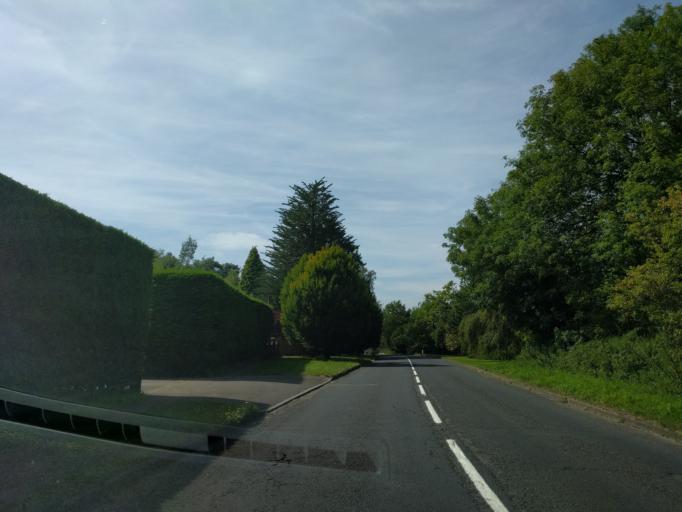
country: GB
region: England
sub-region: Surrey
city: Chilworth
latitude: 51.2157
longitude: -0.5217
